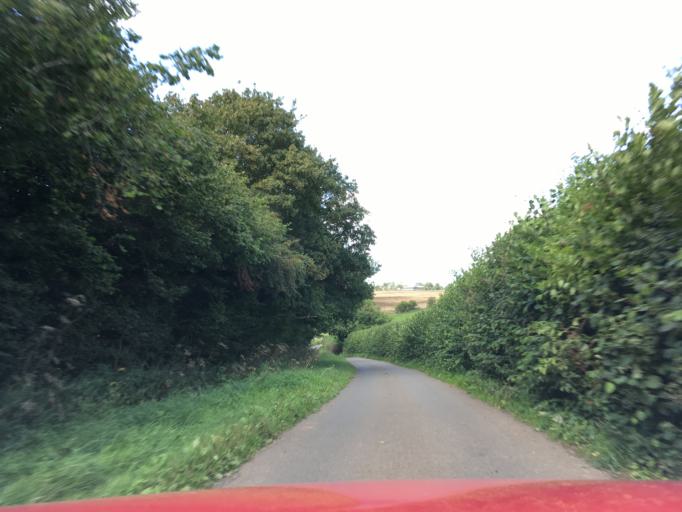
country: GB
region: England
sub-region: Wiltshire
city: Luckington
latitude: 51.6075
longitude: -2.2503
